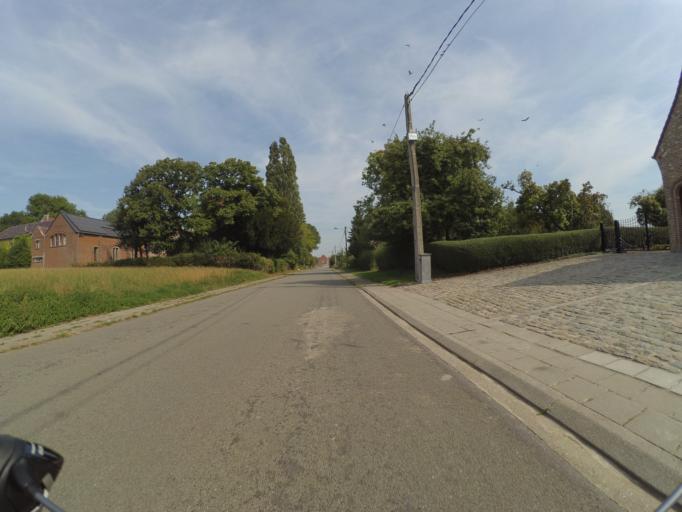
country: BE
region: Wallonia
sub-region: Province du Hainaut
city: Flobecq
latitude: 50.7178
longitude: 3.7371
